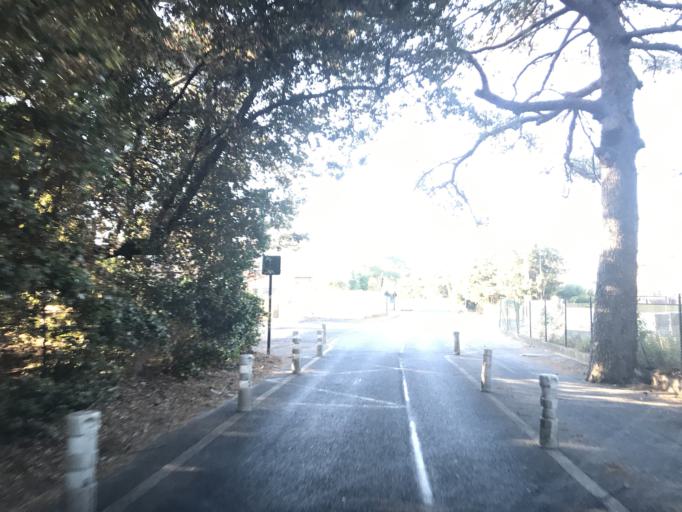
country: FR
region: Provence-Alpes-Cote d'Azur
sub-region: Departement du Var
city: Six-Fours-les-Plages
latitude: 43.0800
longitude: 5.8590
